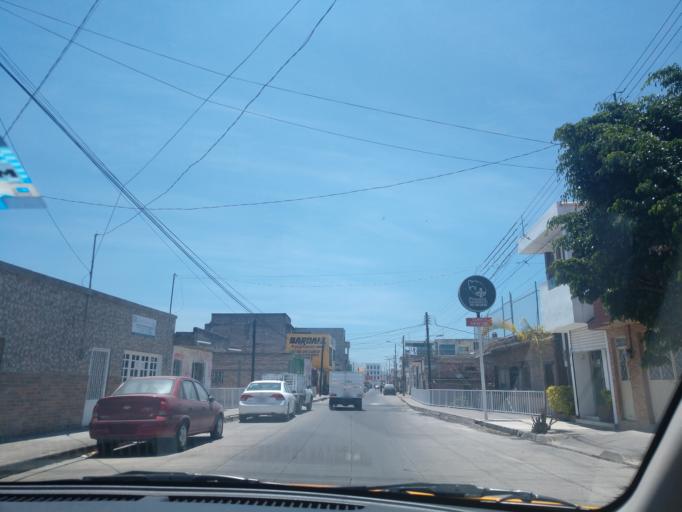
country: MX
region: Nayarit
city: Tepic
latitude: 21.5174
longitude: -104.9005
